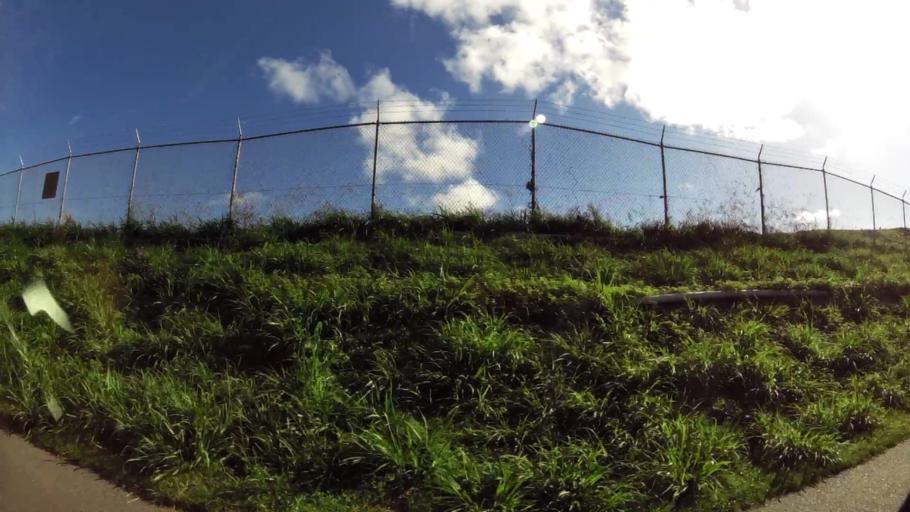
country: TT
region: Tobago
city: Scarborough
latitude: 11.1506
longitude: -60.8451
